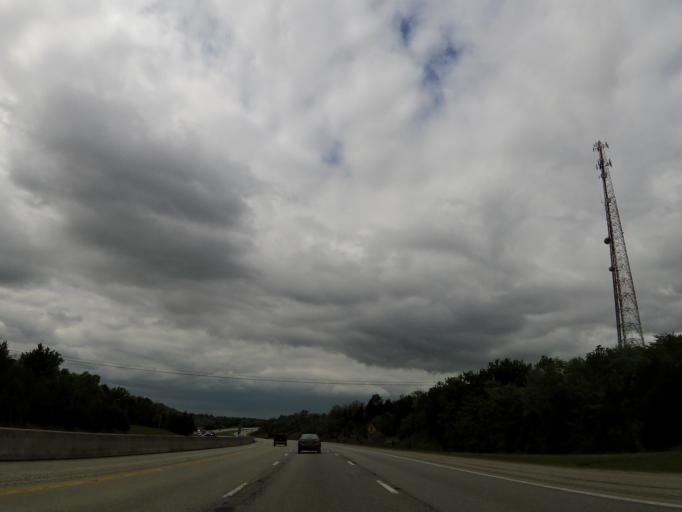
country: US
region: Kentucky
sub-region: Scott County
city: Georgetown
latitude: 38.3806
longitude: -84.5707
